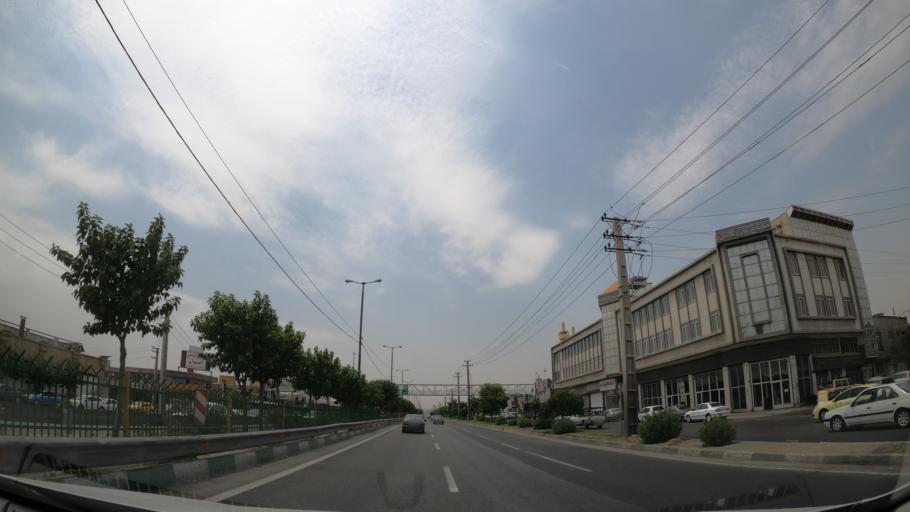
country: IR
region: Tehran
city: Tehran
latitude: 35.6762
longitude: 51.2937
